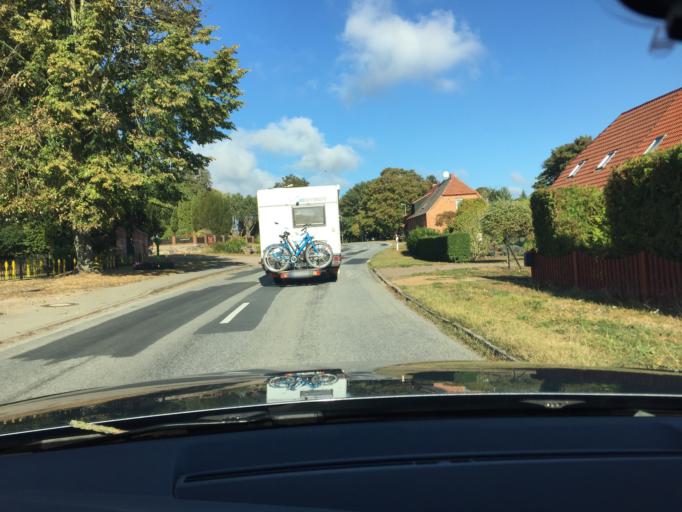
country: DE
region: Mecklenburg-Vorpommern
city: Lalendorf
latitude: 53.6858
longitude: 12.3581
